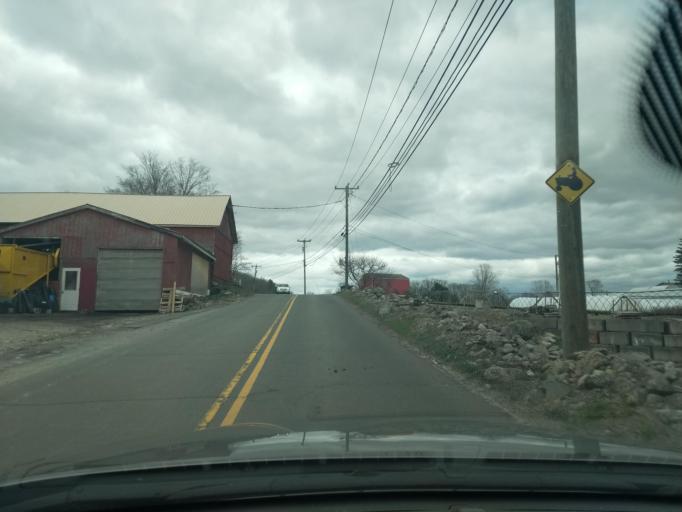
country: US
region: Connecticut
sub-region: Fairfield County
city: Newtown
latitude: 41.3486
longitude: -73.2908
